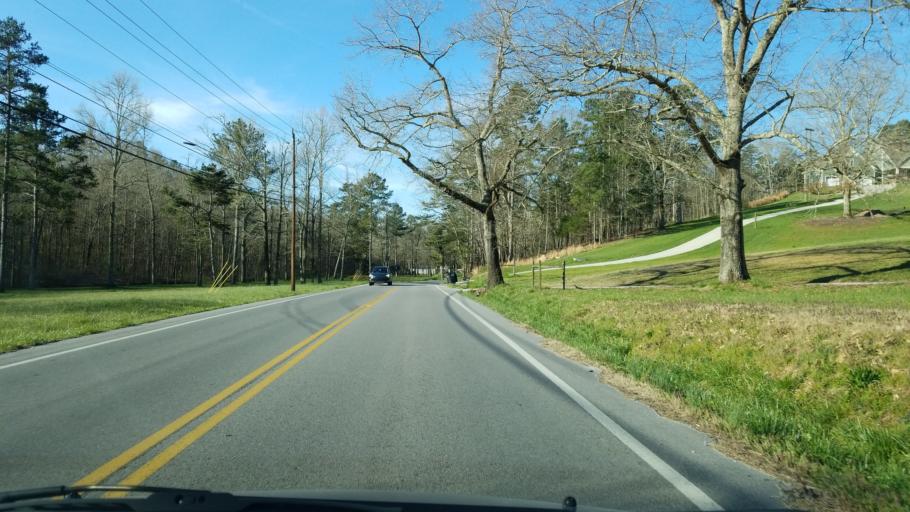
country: US
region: Tennessee
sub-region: Hamilton County
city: East Brainerd
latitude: 35.0111
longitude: -85.1156
